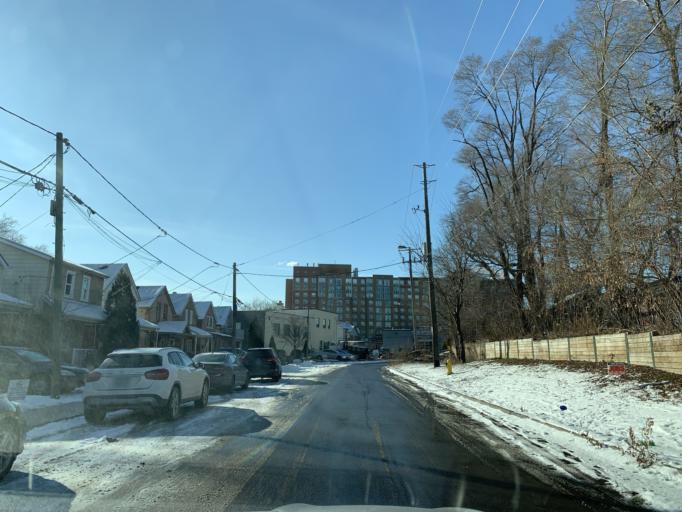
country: CA
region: Ontario
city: Toronto
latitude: 43.6808
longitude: -79.4697
